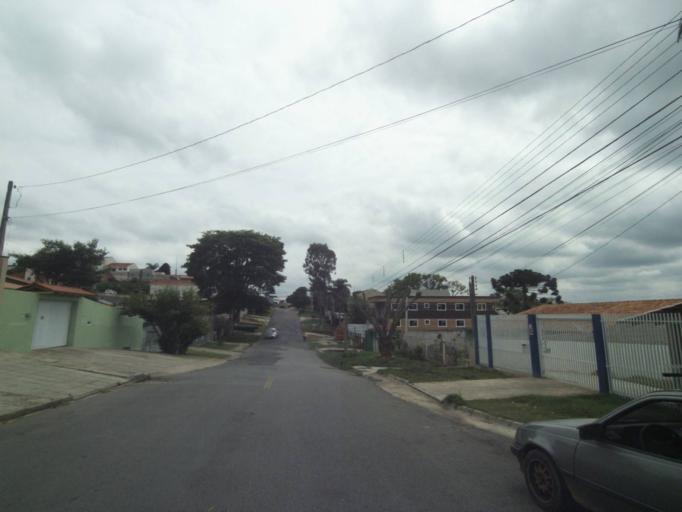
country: BR
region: Parana
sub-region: Curitiba
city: Curitiba
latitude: -25.3914
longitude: -49.2836
